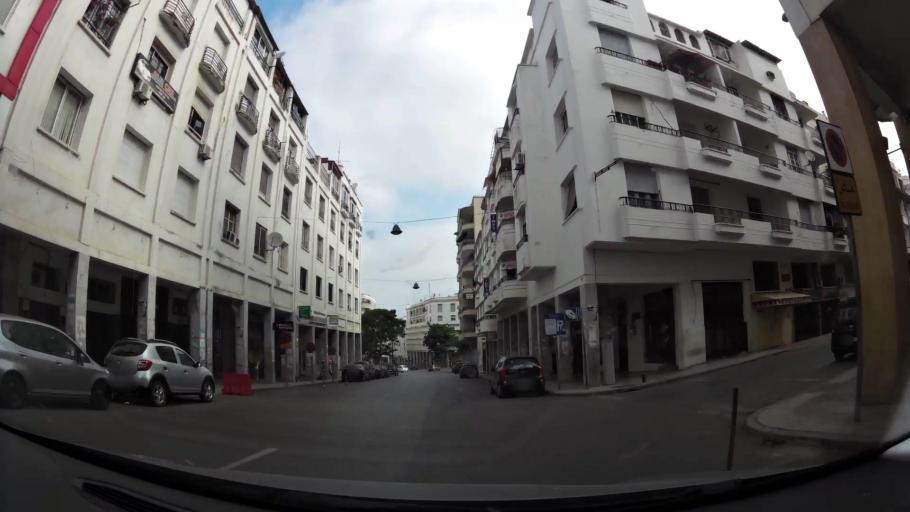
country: MA
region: Rabat-Sale-Zemmour-Zaer
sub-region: Rabat
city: Rabat
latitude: 34.0175
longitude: -6.8341
